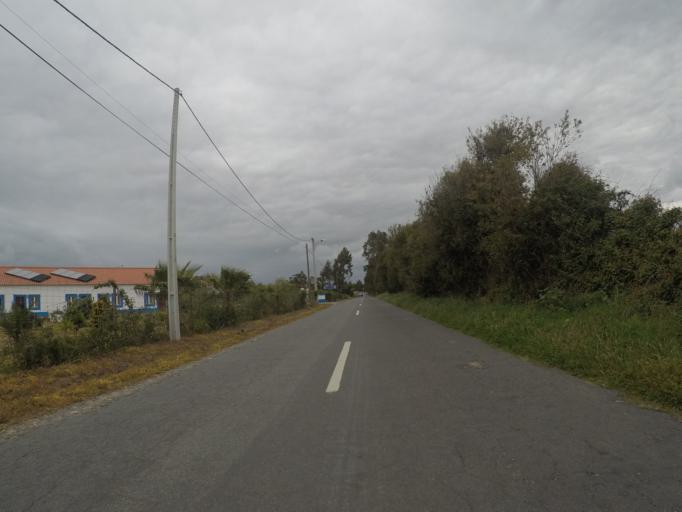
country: PT
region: Beja
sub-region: Odemira
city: Sao Teotonio
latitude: 37.5874
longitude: -8.7780
